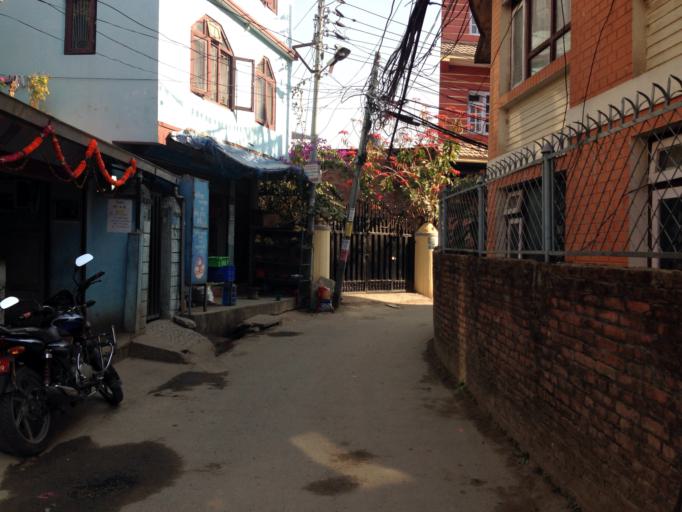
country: NP
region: Central Region
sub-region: Bagmati Zone
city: Kathmandu
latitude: 27.7234
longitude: 85.3239
